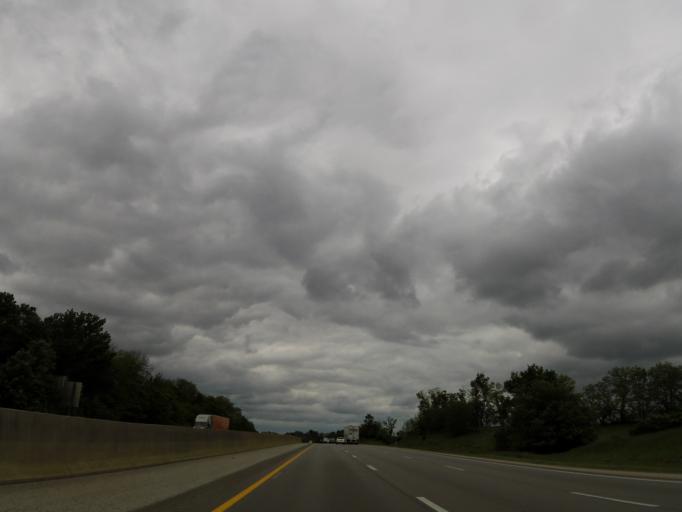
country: US
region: Kentucky
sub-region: Grant County
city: Dry Ridge
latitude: 38.6954
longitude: -84.6011
